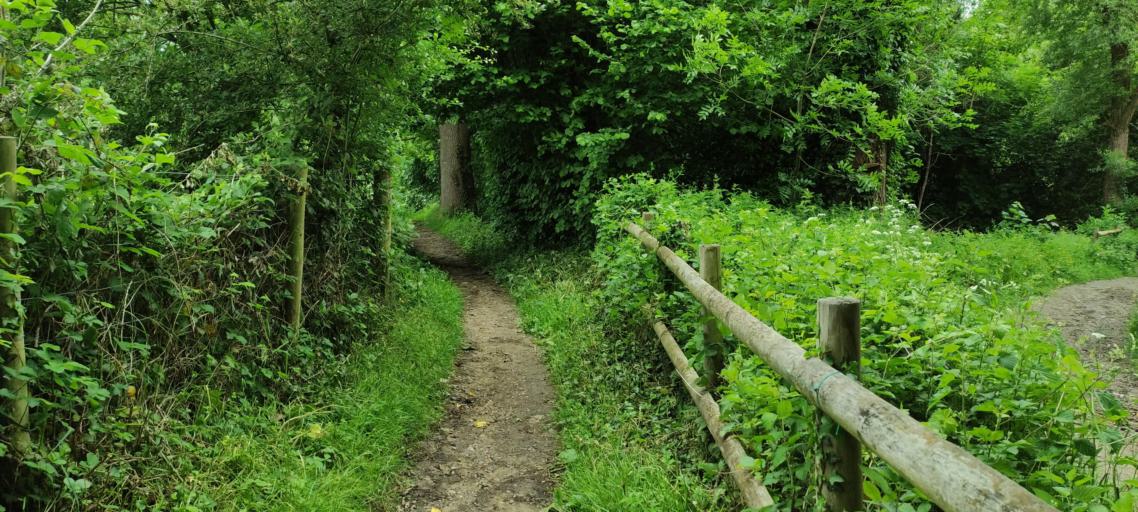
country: GB
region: England
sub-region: Greater London
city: Chislehurst
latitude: 51.4035
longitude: 0.0780
